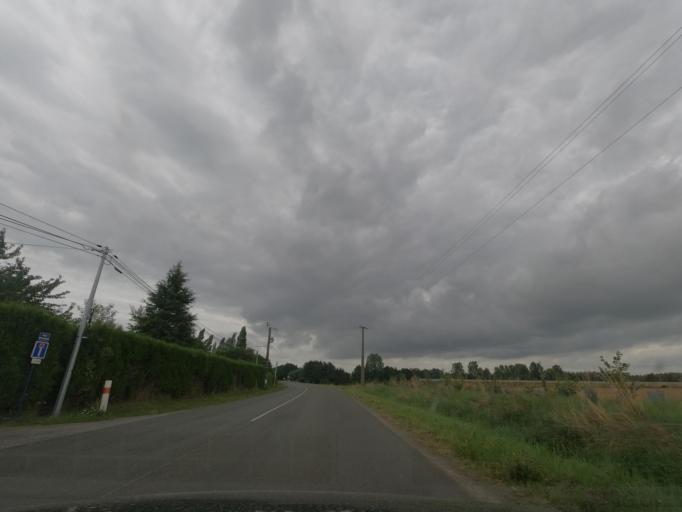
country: FR
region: Lower Normandy
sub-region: Departement de l'Orne
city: Ecouche
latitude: 48.7147
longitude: -0.1100
